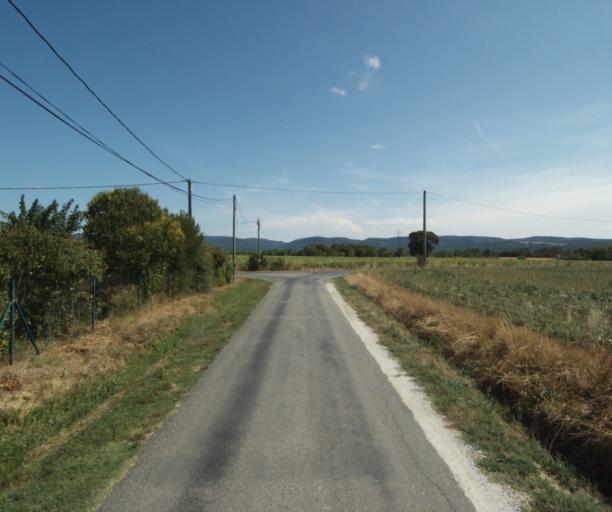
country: FR
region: Midi-Pyrenees
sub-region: Departement de la Haute-Garonne
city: Revel
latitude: 43.4820
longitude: 2.0070
